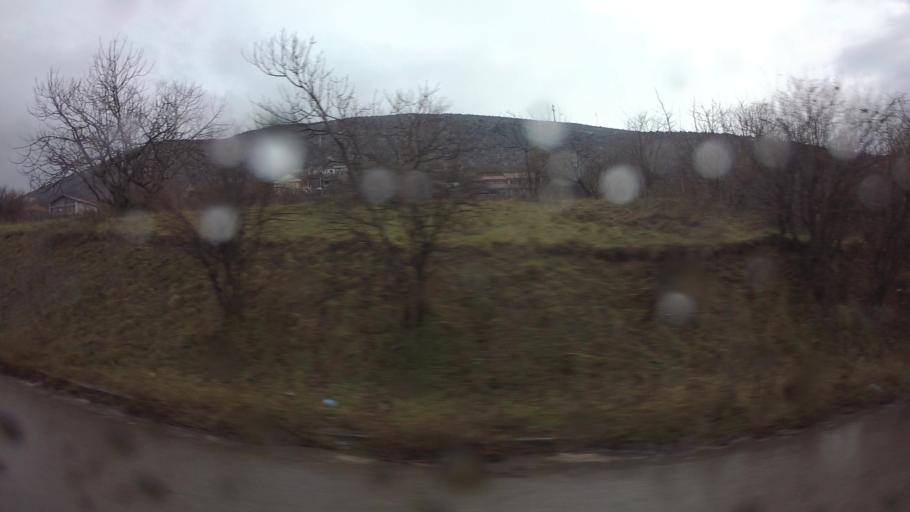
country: BA
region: Federation of Bosnia and Herzegovina
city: Blagaj
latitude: 43.2920
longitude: 17.8586
